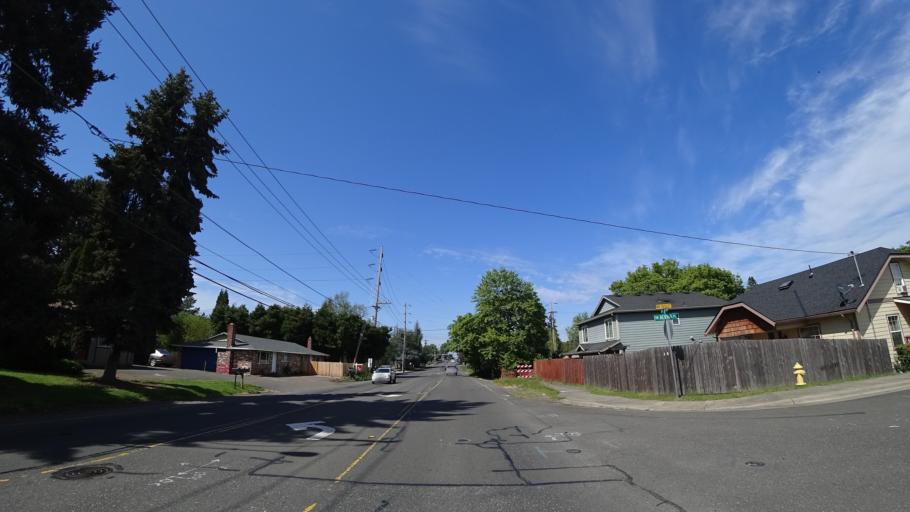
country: US
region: Oregon
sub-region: Washington County
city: Aloha
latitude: 45.4914
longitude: -122.8813
